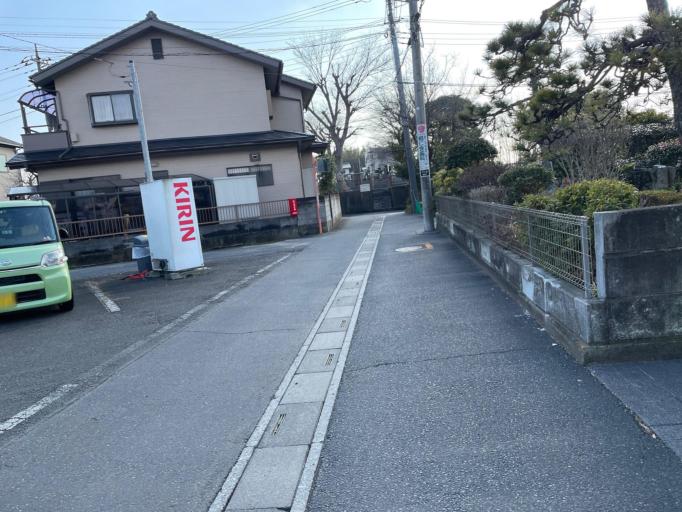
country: JP
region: Saitama
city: Yashio-shi
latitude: 35.8046
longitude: 139.8595
